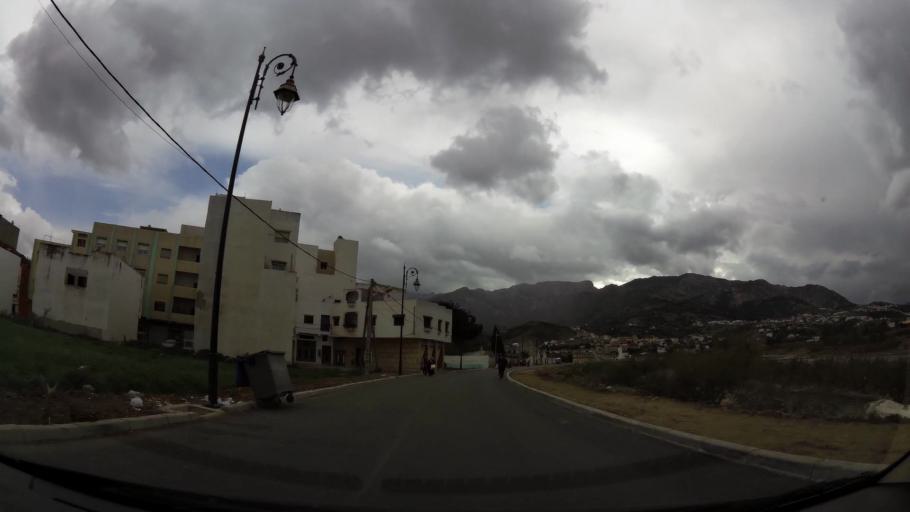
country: MA
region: Tanger-Tetouan
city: Tetouan
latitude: 35.5600
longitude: -5.3499
